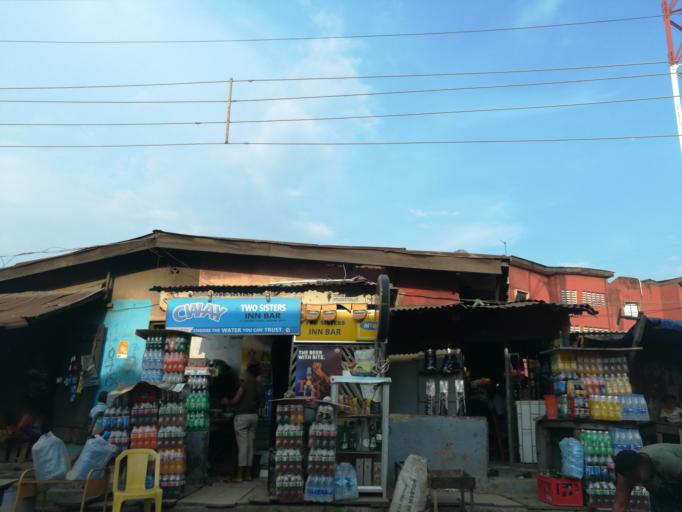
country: NG
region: Lagos
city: Ojota
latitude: 6.5889
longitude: 3.3962
